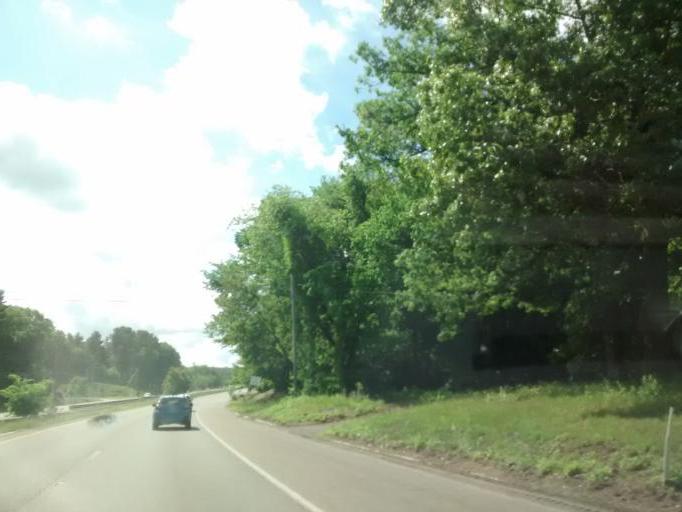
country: US
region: Massachusetts
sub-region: Worcester County
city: Sutton
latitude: 42.1569
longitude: -71.7306
